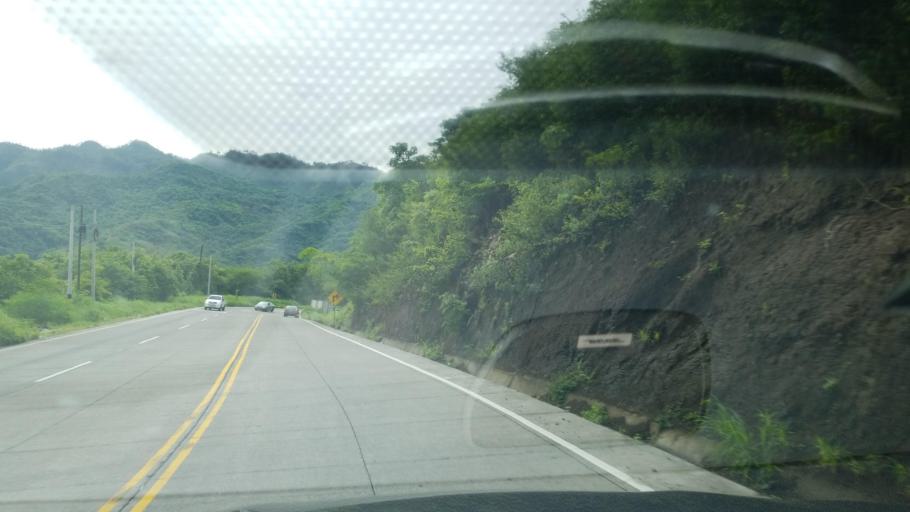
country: HN
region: Francisco Morazan
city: El Porvenir
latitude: 13.7066
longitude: -87.3169
